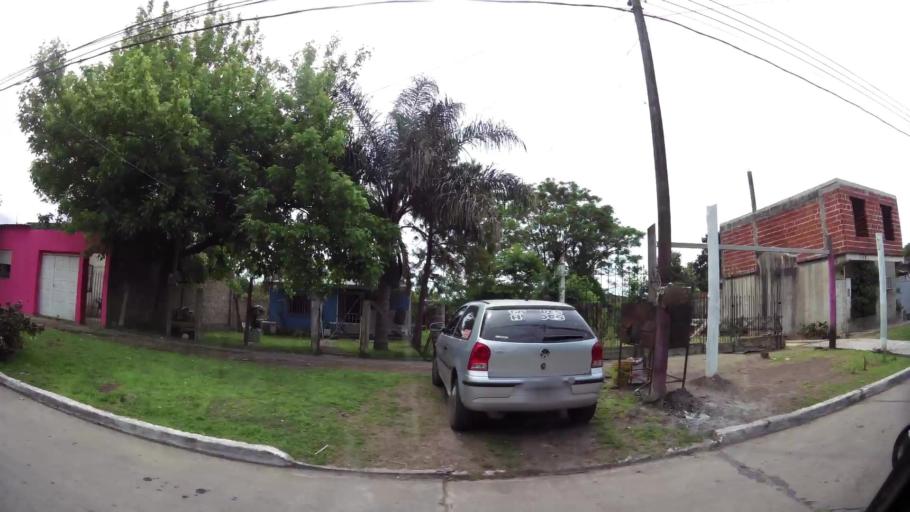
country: AR
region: Buenos Aires
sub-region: Partido de Quilmes
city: Quilmes
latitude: -34.7607
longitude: -58.2666
